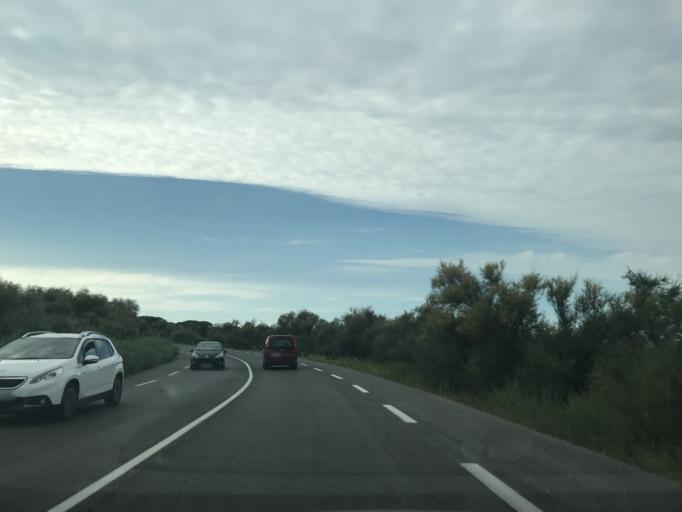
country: FR
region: Languedoc-Roussillon
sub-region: Departement du Gard
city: Le Grau-du-Roi
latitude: 43.5530
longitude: 4.1313
